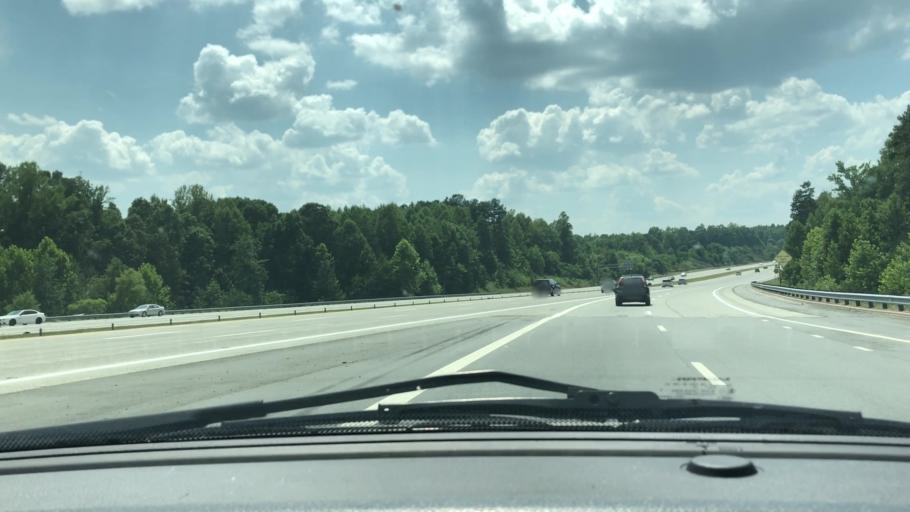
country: US
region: North Carolina
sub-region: Guilford County
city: Pleasant Garden
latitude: 35.9974
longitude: -79.7585
